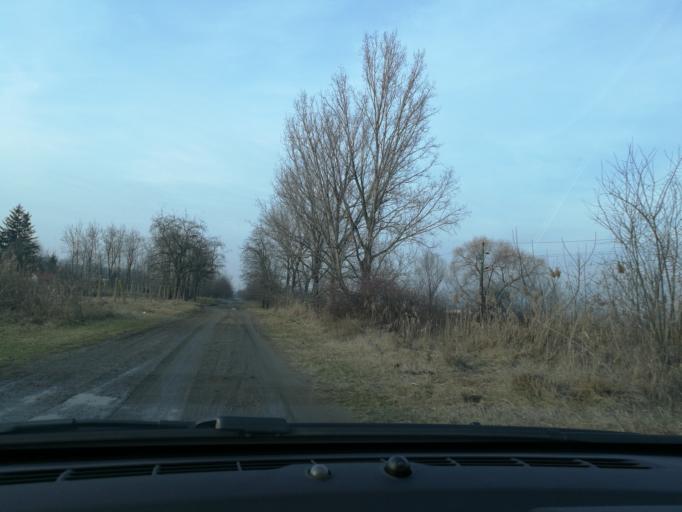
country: HU
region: Szabolcs-Szatmar-Bereg
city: Nyiregyhaza
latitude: 47.9602
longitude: 21.6924
